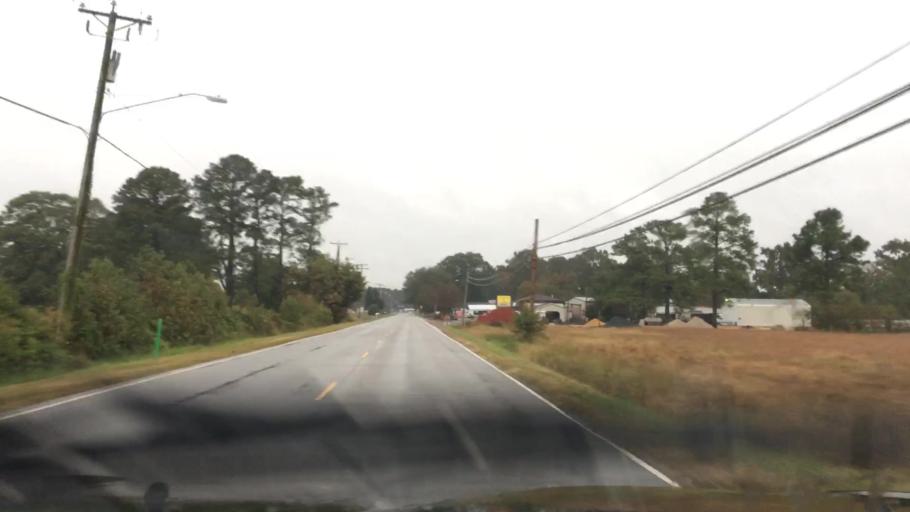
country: US
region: North Carolina
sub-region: Currituck County
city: Moyock
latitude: 36.6697
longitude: -76.2269
